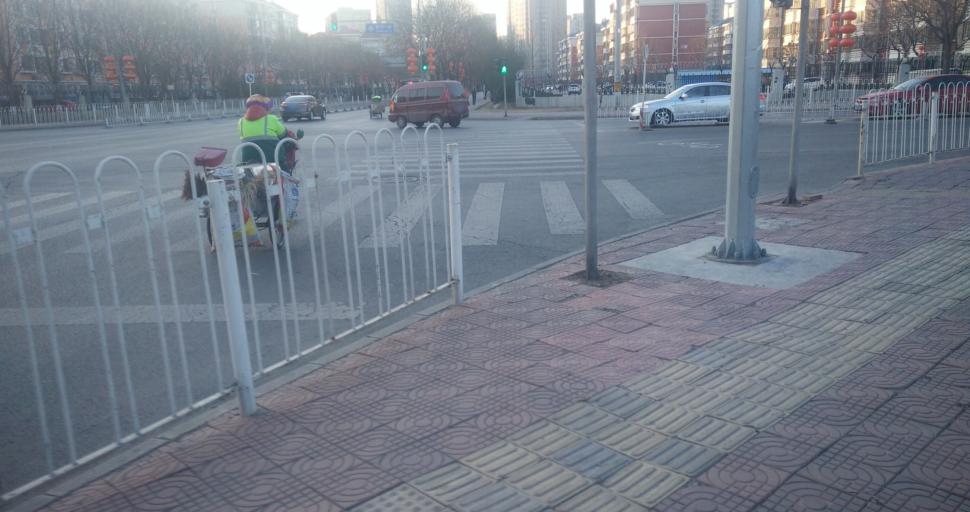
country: CN
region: Beijing
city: Yinghai
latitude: 39.7590
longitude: 116.4967
